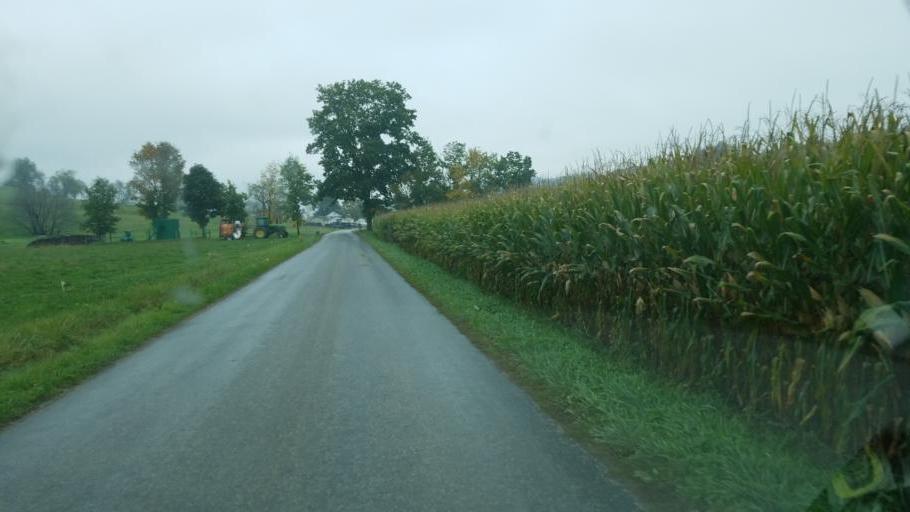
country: US
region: Ohio
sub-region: Tuscarawas County
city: Sugarcreek
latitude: 40.5876
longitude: -81.7448
